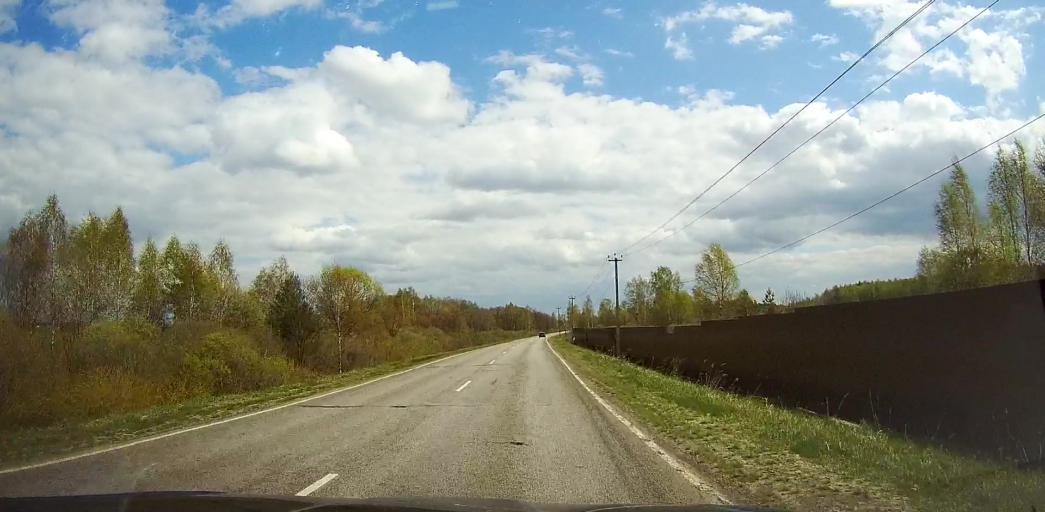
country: RU
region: Moskovskaya
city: Davydovo
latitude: 55.5510
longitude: 38.7945
